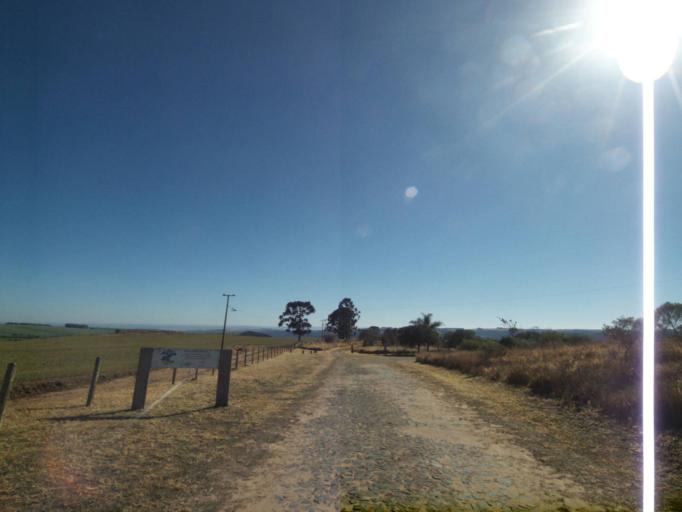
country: BR
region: Parana
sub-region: Tibagi
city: Tibagi
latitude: -24.5698
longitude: -50.2663
